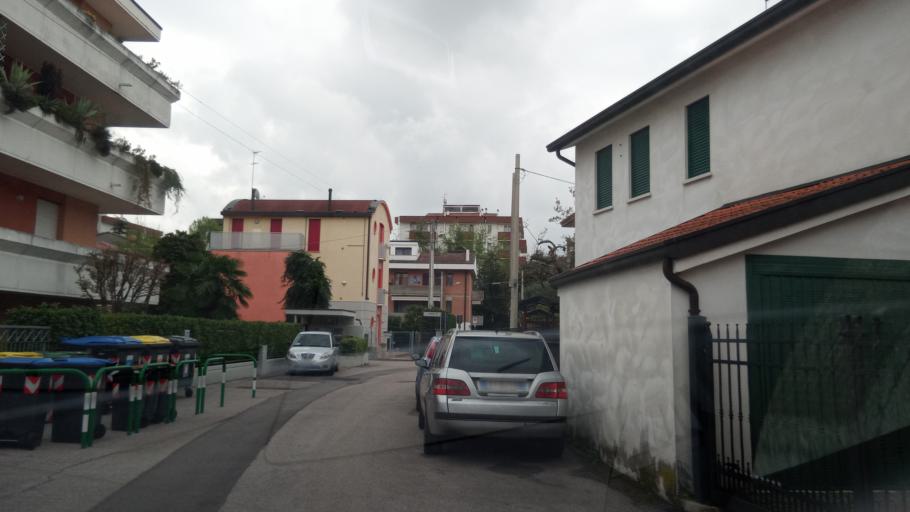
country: IT
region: Veneto
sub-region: Provincia di Padova
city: Cadoneghe
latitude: 45.4241
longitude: 11.9121
